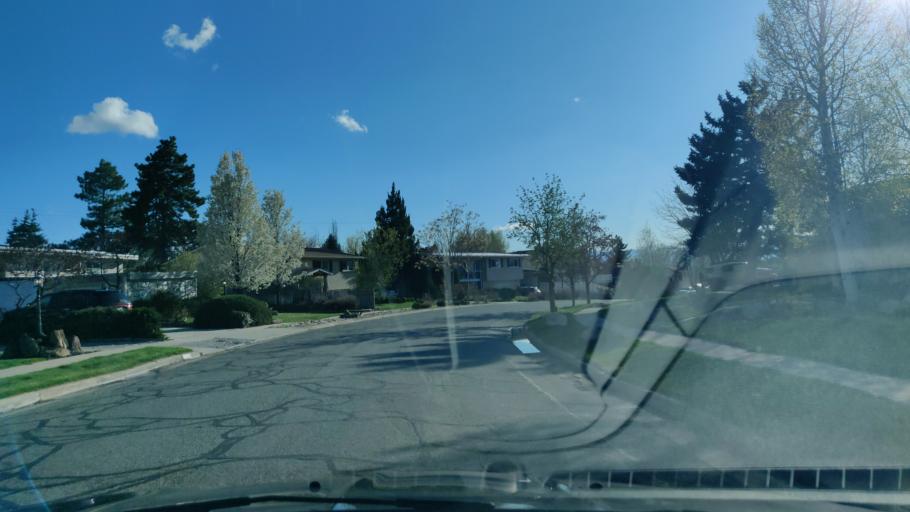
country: US
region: Utah
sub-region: Salt Lake County
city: Cottonwood Heights
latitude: 40.6173
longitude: -111.8226
